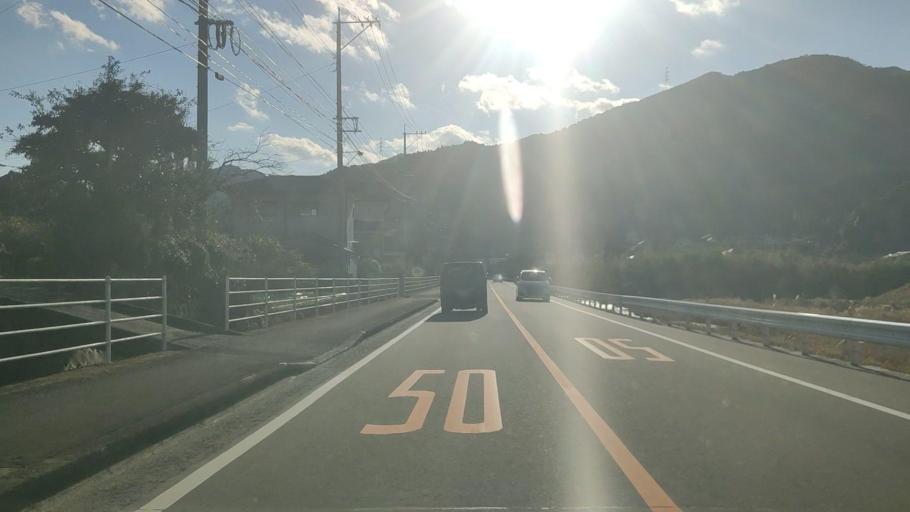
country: JP
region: Saga Prefecture
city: Saga-shi
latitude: 33.3552
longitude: 130.2505
